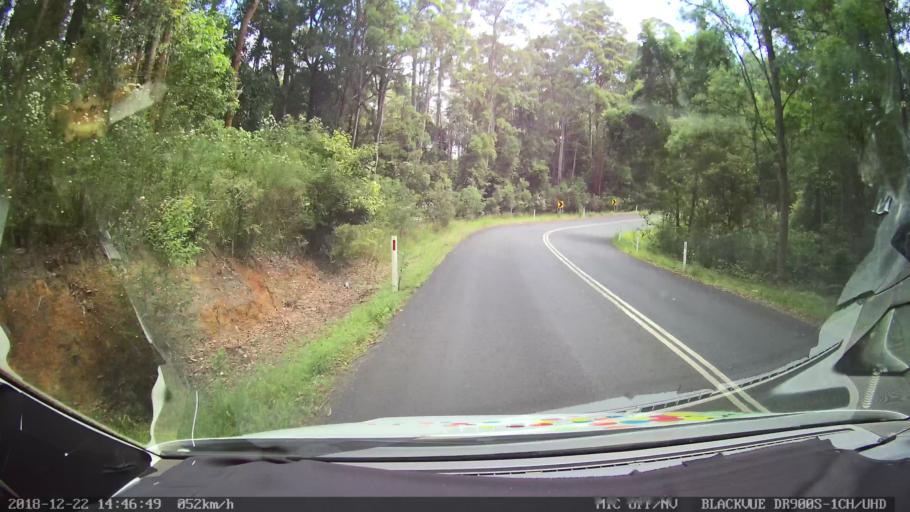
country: AU
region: New South Wales
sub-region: Bellingen
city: Dorrigo
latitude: -30.1750
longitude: 152.5603
